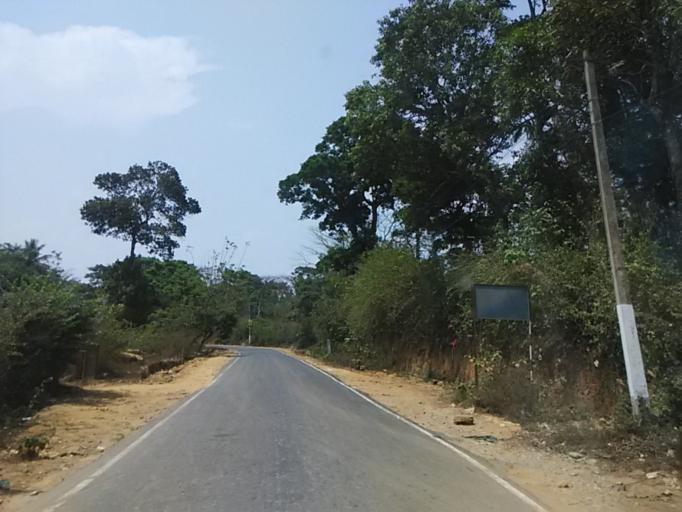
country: IN
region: Karnataka
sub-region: Kodagu
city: Virarajendrapet
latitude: 12.1446
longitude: 75.7957
